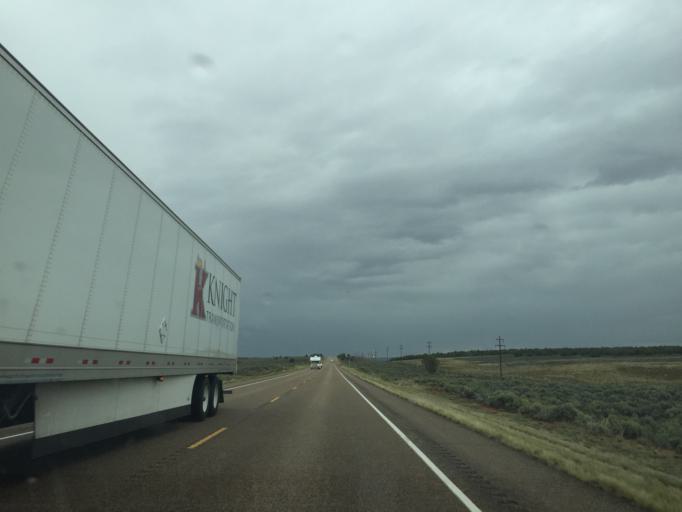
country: US
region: Utah
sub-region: Kane County
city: Kanab
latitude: 37.1383
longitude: -112.0797
